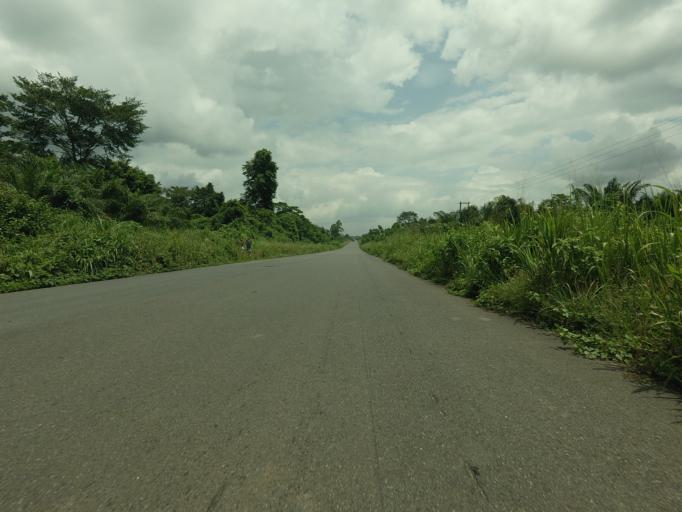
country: GH
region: Volta
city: Ho
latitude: 6.5711
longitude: 0.2732
